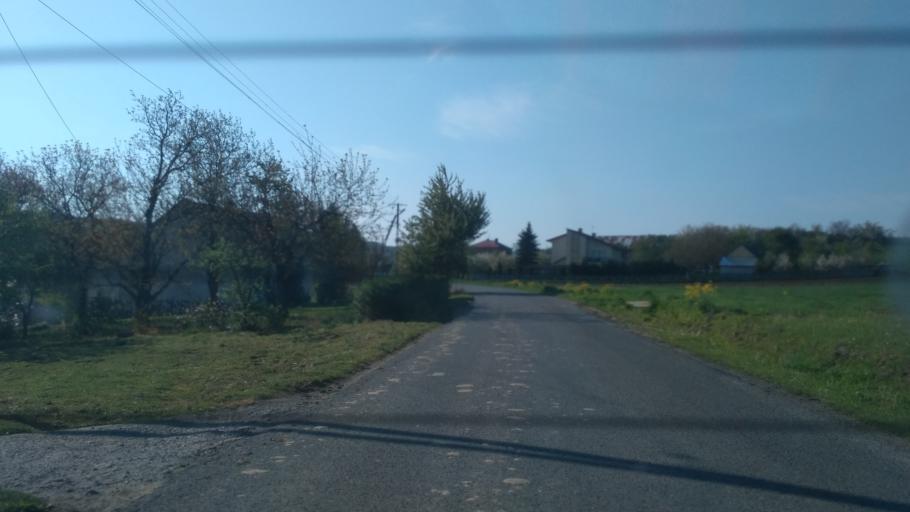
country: PL
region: Subcarpathian Voivodeship
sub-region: Powiat jaroslawski
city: Pruchnik
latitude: 49.8972
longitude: 22.5527
